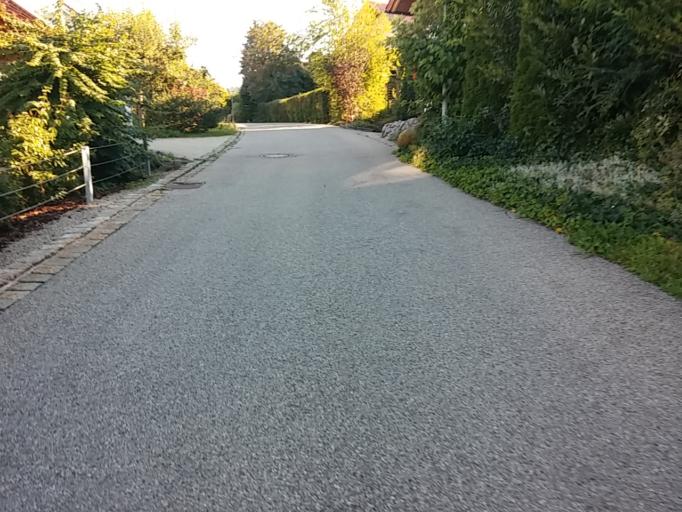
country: DE
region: Bavaria
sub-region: Swabia
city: Wiggensbach
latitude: 47.7437
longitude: 10.2307
